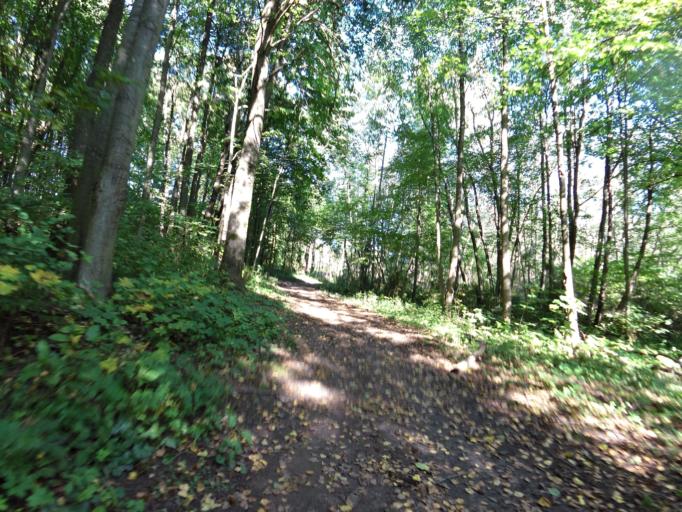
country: LT
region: Vilnius County
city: Pilaite
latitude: 54.7000
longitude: 25.1882
